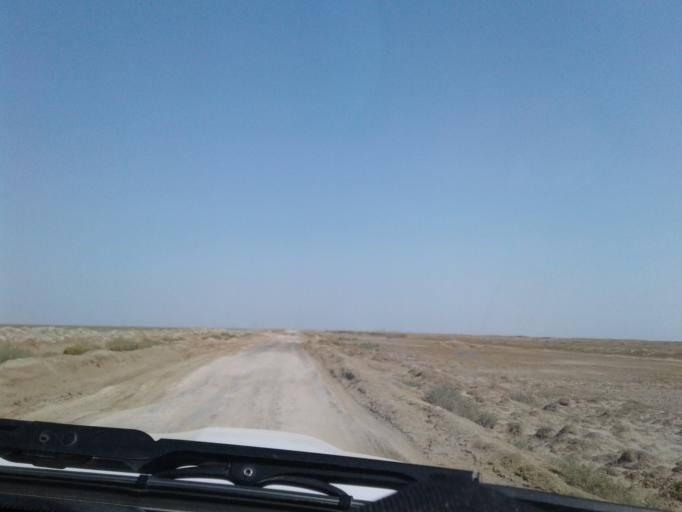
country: IR
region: Golestan
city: Gomishan
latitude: 37.8286
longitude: 53.9215
